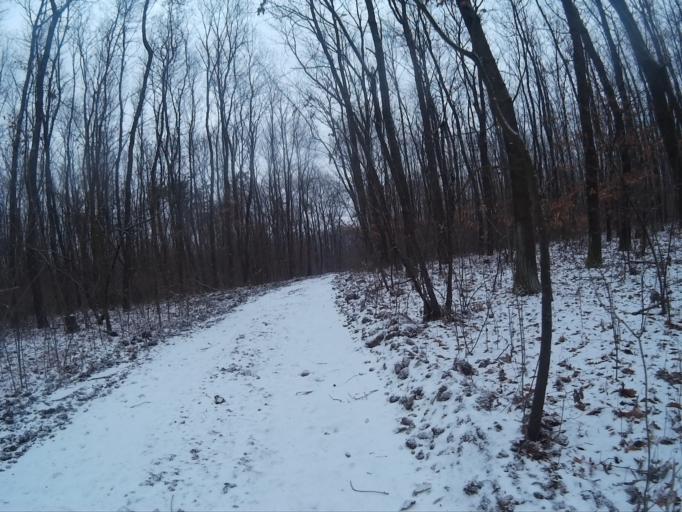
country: HU
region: Borsod-Abauj-Zemplen
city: Halmaj
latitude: 48.3799
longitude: 20.9045
